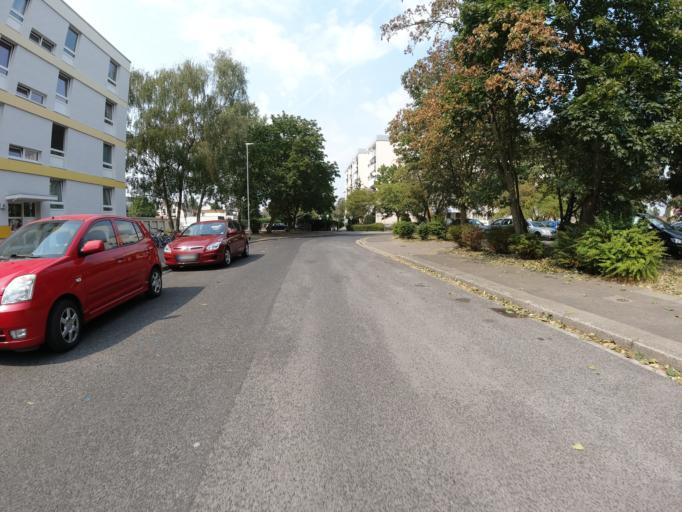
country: DE
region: North Rhine-Westphalia
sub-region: Regierungsbezirk Dusseldorf
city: Moers
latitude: 51.4400
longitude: 6.6431
